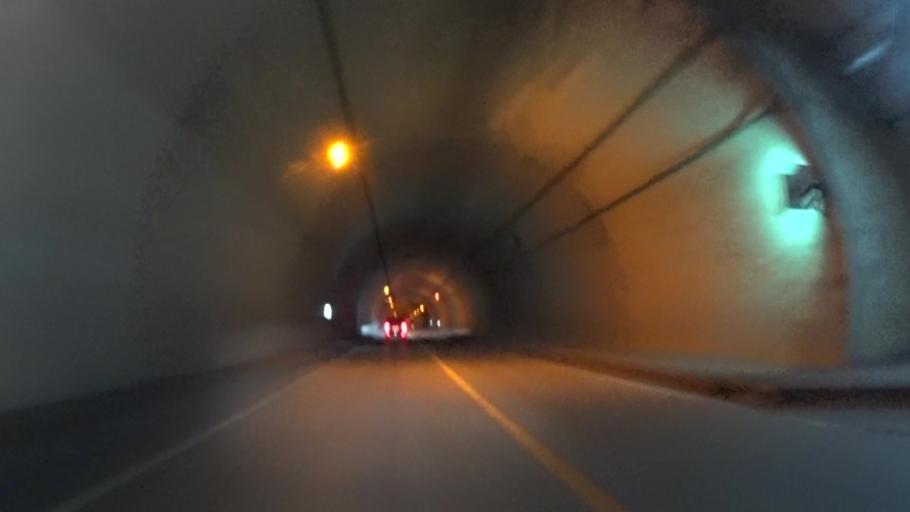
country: JP
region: Kyoto
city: Fukuchiyama
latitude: 35.4040
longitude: 135.0382
